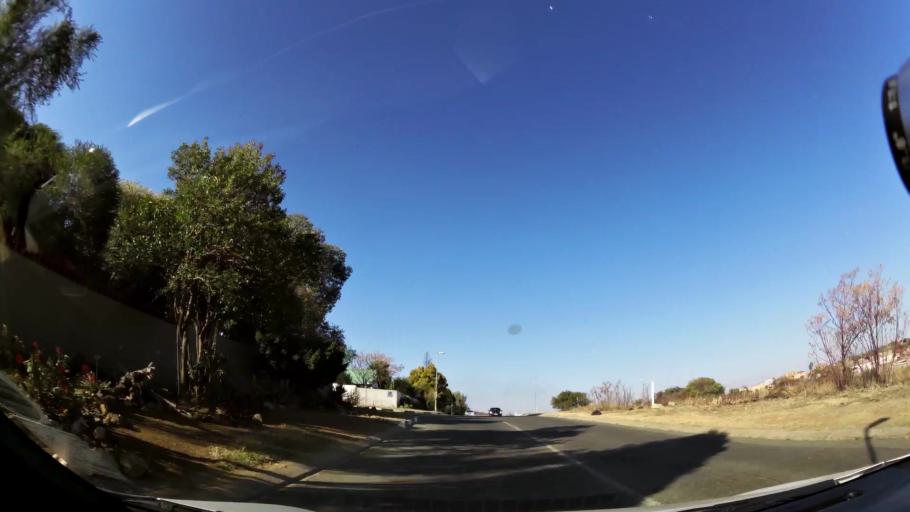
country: ZA
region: Gauteng
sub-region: City of Johannesburg Metropolitan Municipality
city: Johannesburg
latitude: -26.3020
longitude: 28.0582
